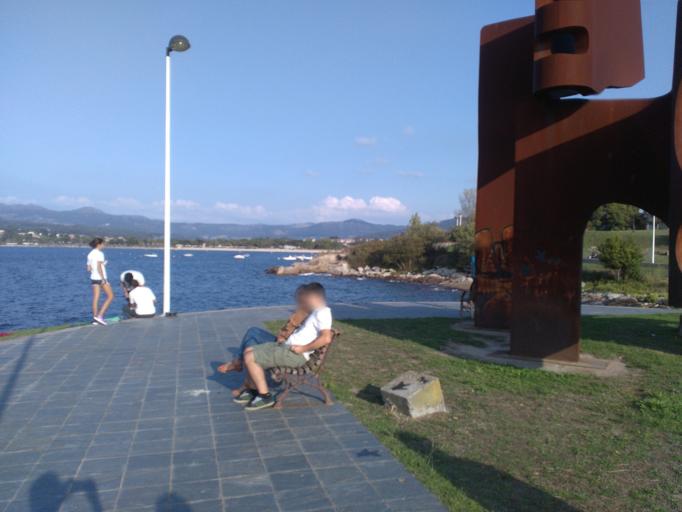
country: ES
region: Galicia
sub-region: Provincia de Pontevedra
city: Baiona
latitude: 42.1160
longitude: -8.8375
